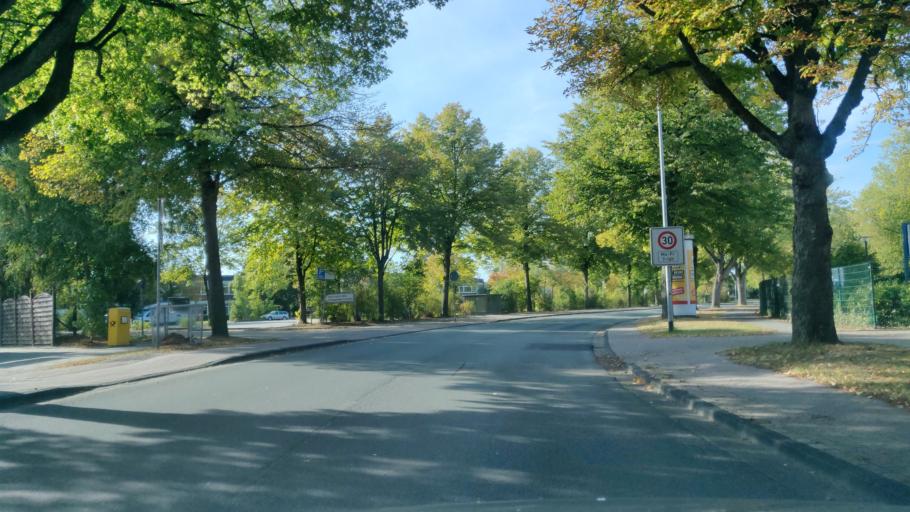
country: DE
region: Lower Saxony
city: Leer
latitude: 53.2260
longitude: 7.4442
